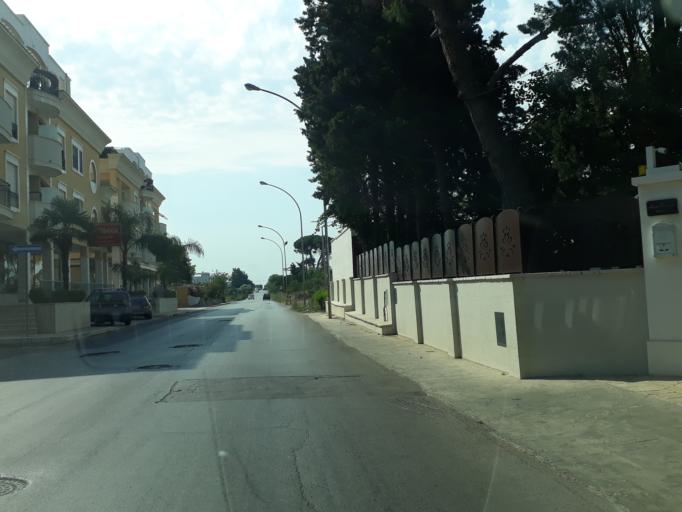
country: IT
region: Apulia
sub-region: Provincia di Brindisi
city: Carovigno
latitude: 40.6992
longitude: 17.6650
